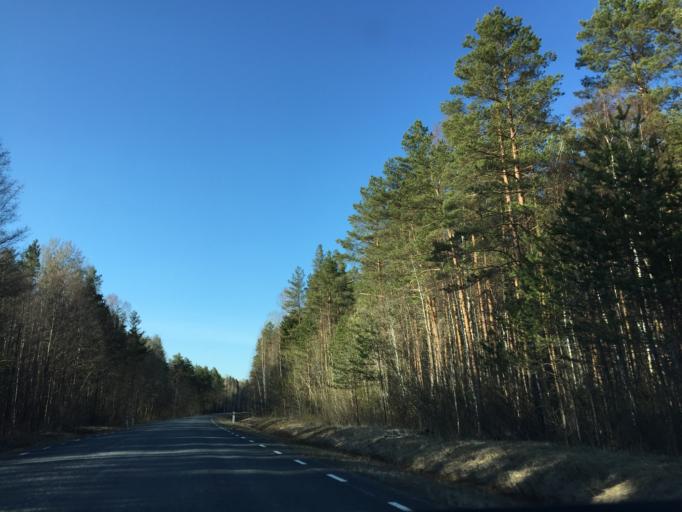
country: RU
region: Pskov
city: Gdov
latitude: 59.0516
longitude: 27.7027
